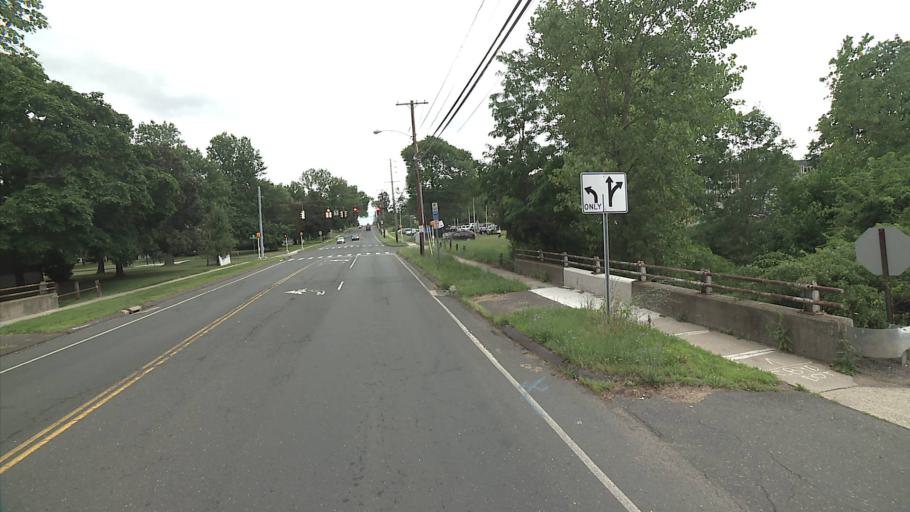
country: US
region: Connecticut
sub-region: Hartford County
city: Wethersfield
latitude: 41.7221
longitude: -72.6795
